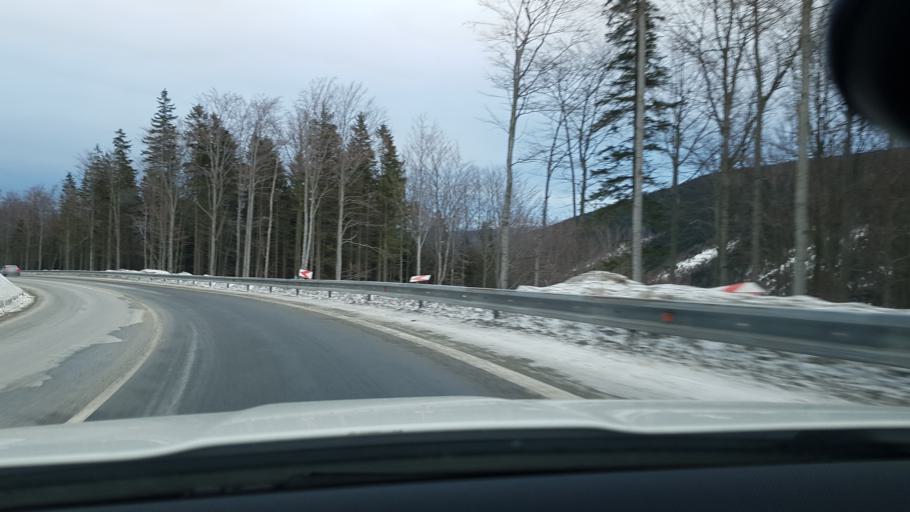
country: CZ
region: Olomoucky
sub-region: Okres Sumperk
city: Loucna nad Desnou
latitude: 50.1362
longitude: 17.1593
